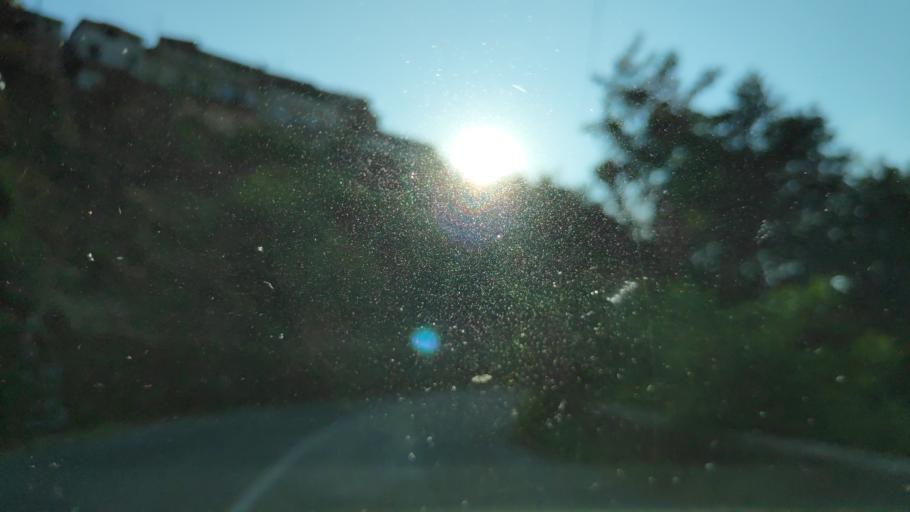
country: IT
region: Calabria
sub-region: Provincia di Catanzaro
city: Satriano
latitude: 38.6700
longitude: 16.4840
